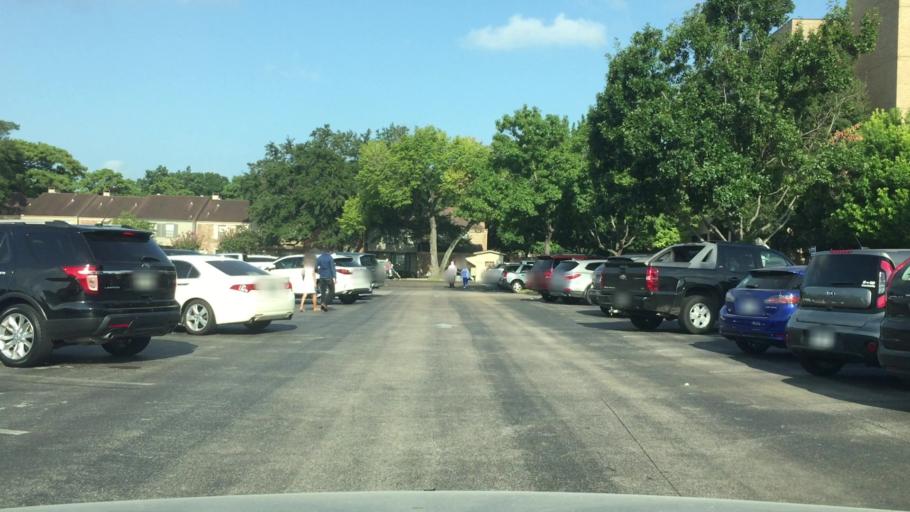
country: US
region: Texas
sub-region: Harris County
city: Hunters Creek Village
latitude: 29.7817
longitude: -95.4594
